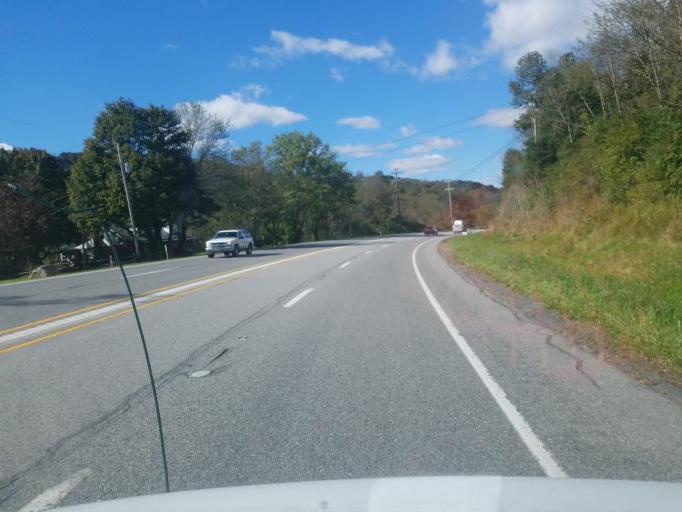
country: US
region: Pennsylvania
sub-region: Bedford County
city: Earlston
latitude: 40.0077
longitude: -78.3099
